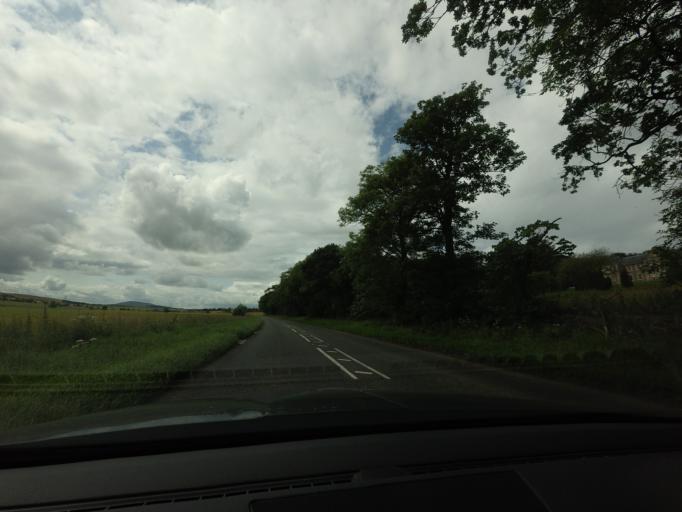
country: GB
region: Scotland
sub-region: Aberdeenshire
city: Whitehills
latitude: 57.6616
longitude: -2.5875
